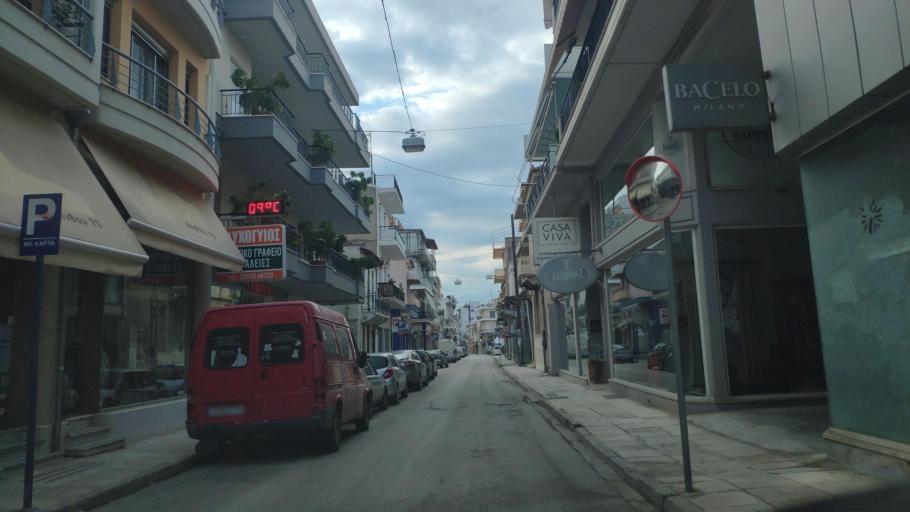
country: GR
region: Peloponnese
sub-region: Nomos Argolidos
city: Argos
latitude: 37.6379
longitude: 22.7289
